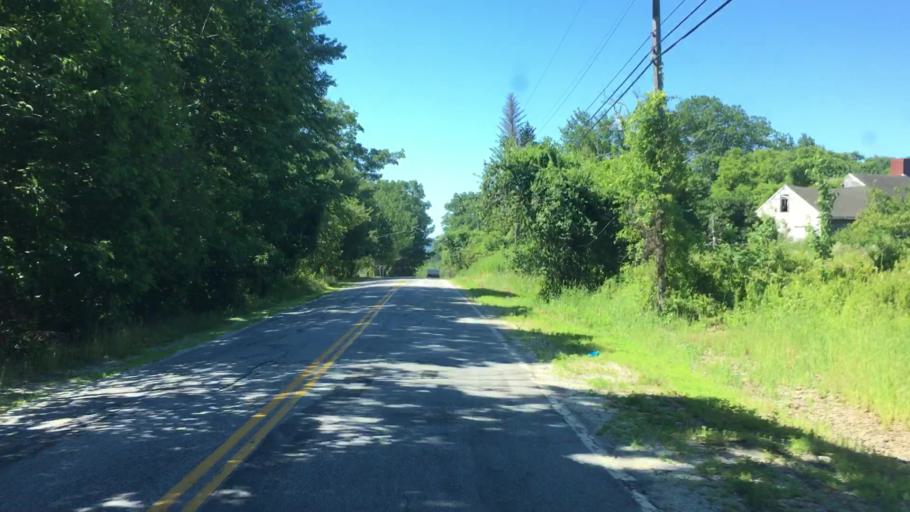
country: US
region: Maine
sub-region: Hancock County
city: Sedgwick
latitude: 44.3197
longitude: -68.6100
